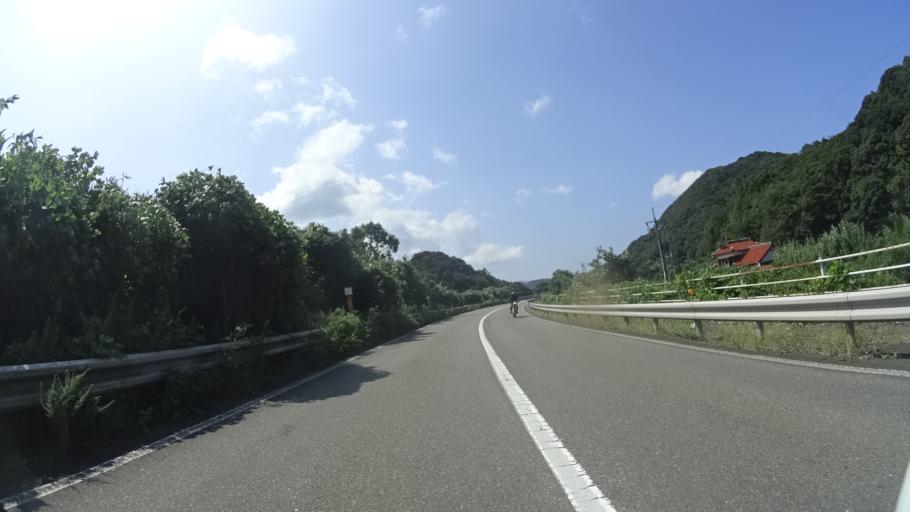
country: JP
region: Shimane
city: Masuda
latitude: 34.6566
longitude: 131.6762
